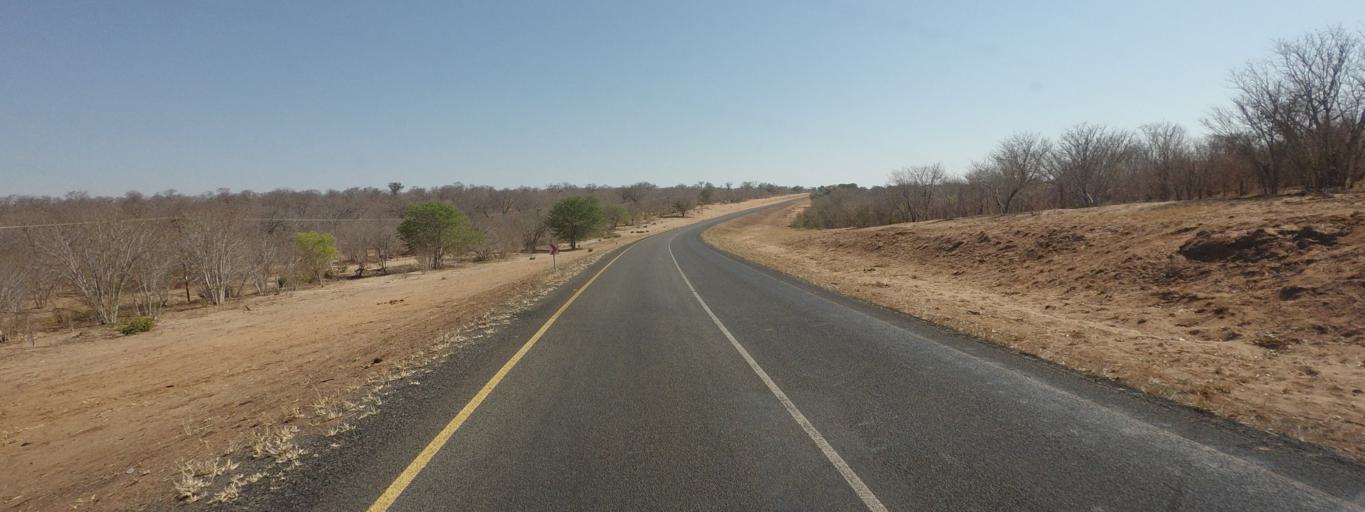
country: BW
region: North West
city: Kasane
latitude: -17.8779
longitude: 25.2127
